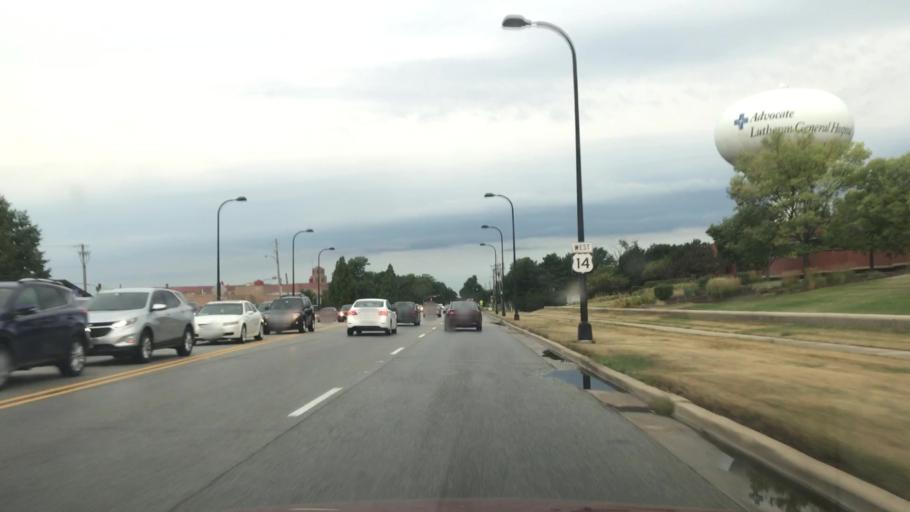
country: US
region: Illinois
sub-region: Cook County
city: Park Ridge
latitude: 42.0398
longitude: -87.8503
